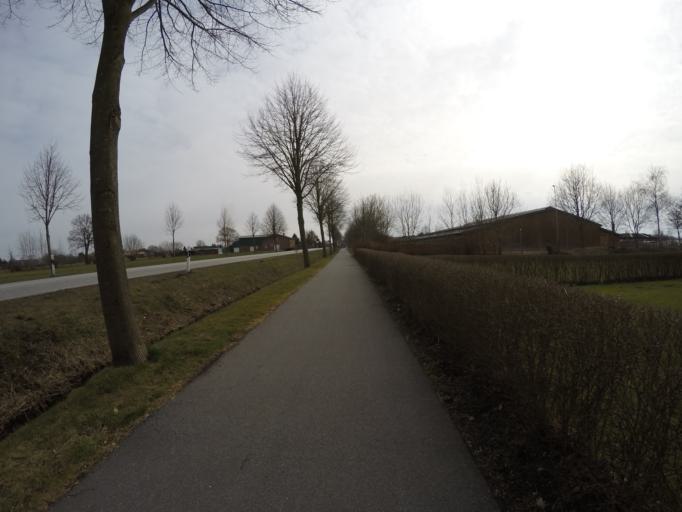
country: DE
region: Schleswig-Holstein
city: Bilsen
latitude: 53.7758
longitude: 9.8754
